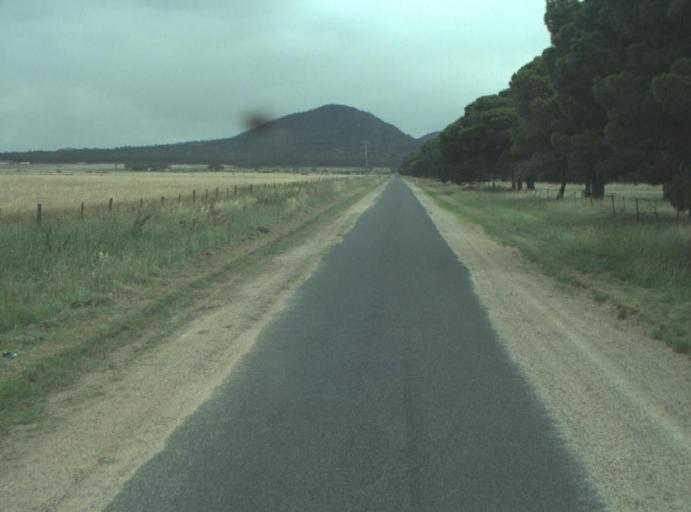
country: AU
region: Victoria
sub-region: Greater Geelong
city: Lara
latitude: -37.9939
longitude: 144.4204
